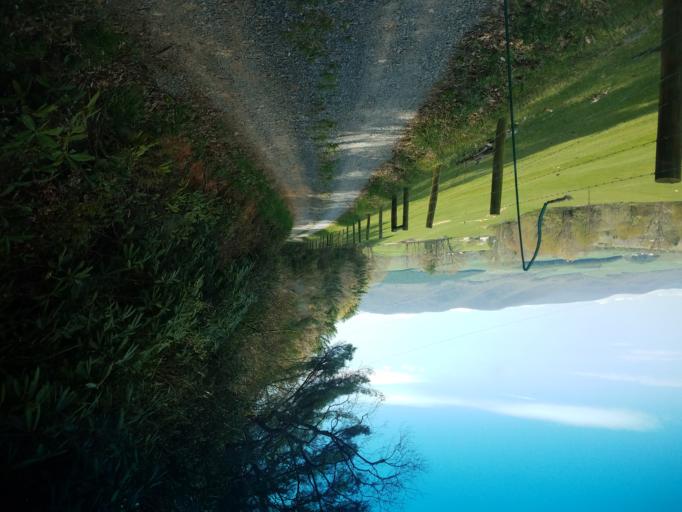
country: US
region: Virginia
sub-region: Smyth County
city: Marion
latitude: 36.7826
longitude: -81.4635
